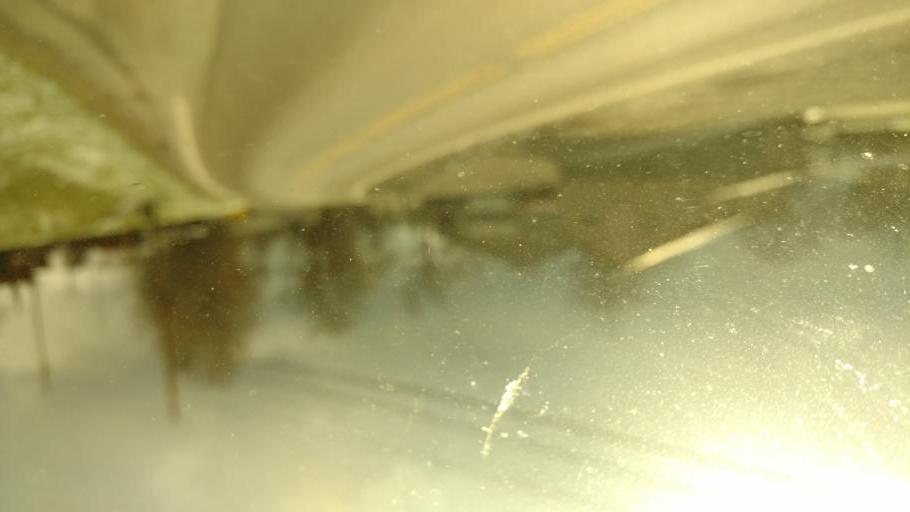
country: US
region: Ohio
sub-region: Holmes County
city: Millersburg
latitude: 40.5173
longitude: -81.8027
